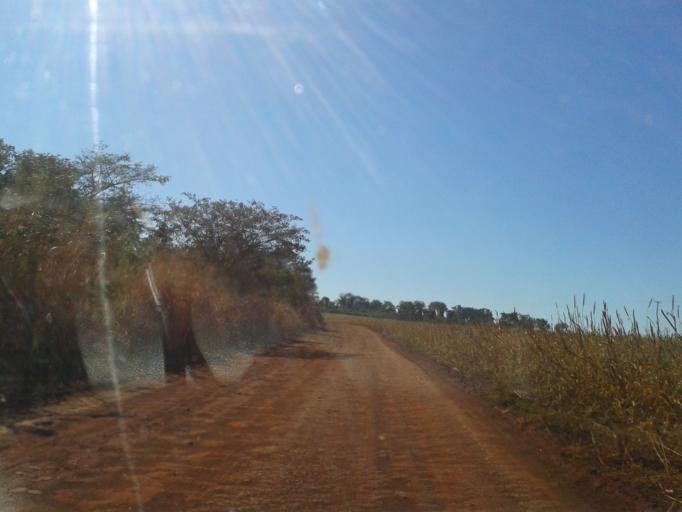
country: BR
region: Minas Gerais
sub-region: Centralina
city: Centralina
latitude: -18.5897
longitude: -49.1527
